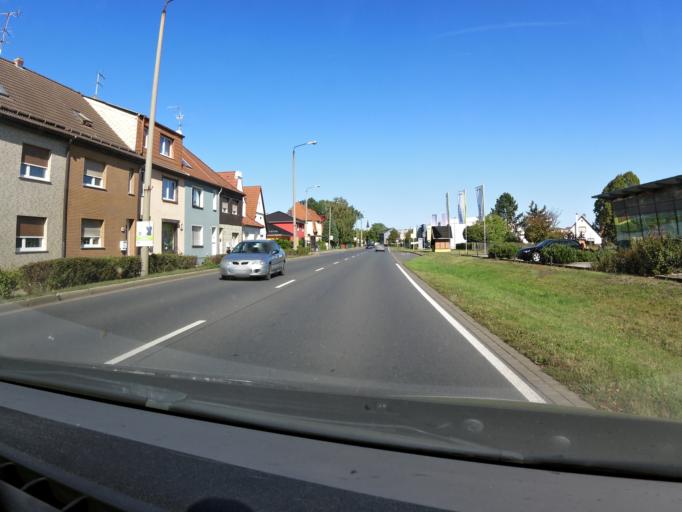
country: DE
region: Thuringia
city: Nordhausen
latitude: 51.4859
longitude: 10.8038
